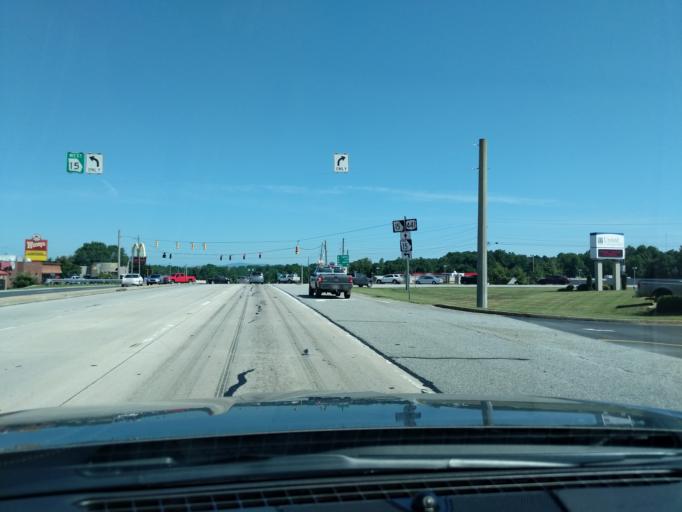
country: US
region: Georgia
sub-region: Habersham County
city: Cornelia
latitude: 34.5098
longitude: -83.5451
